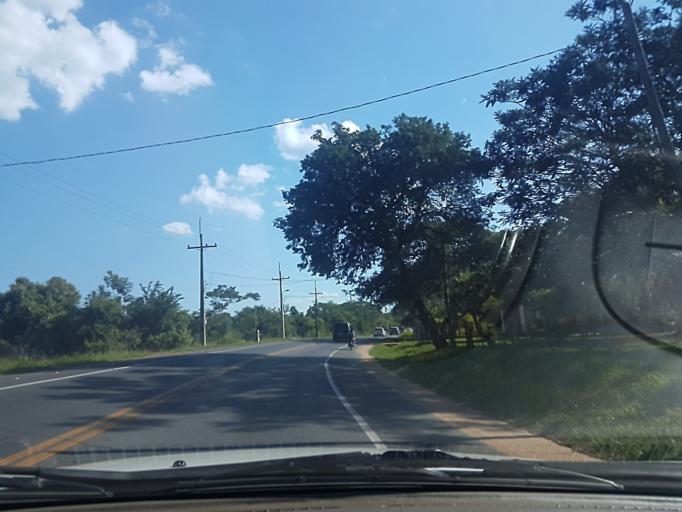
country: PY
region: Central
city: Aregua
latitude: -25.2298
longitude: -57.4180
